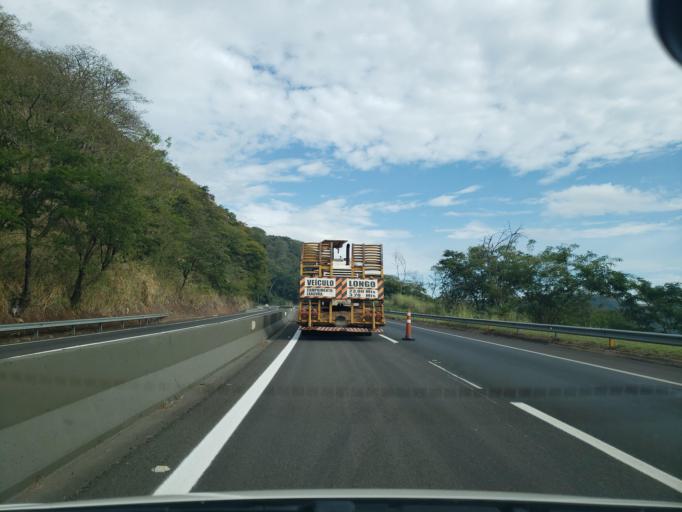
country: BR
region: Sao Paulo
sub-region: Dois Corregos
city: Dois Corregos
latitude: -22.2490
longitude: -48.3438
